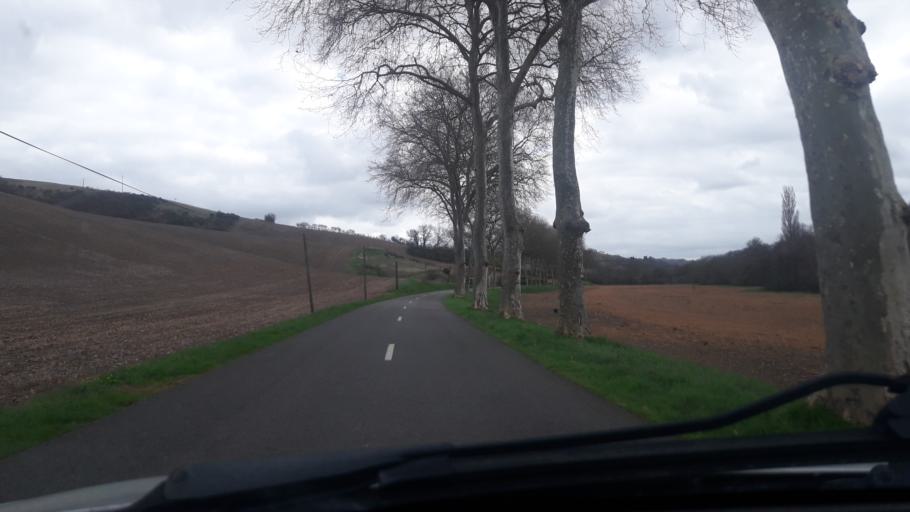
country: FR
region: Midi-Pyrenees
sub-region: Departement de la Haute-Garonne
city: Montesquieu-Volvestre
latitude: 43.2362
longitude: 1.2747
